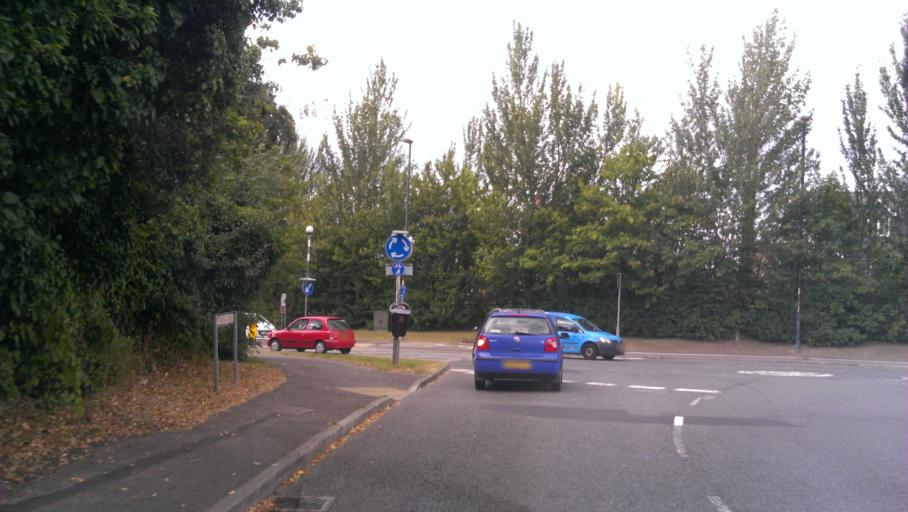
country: GB
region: England
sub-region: Kent
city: Strood
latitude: 51.4087
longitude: 0.4989
